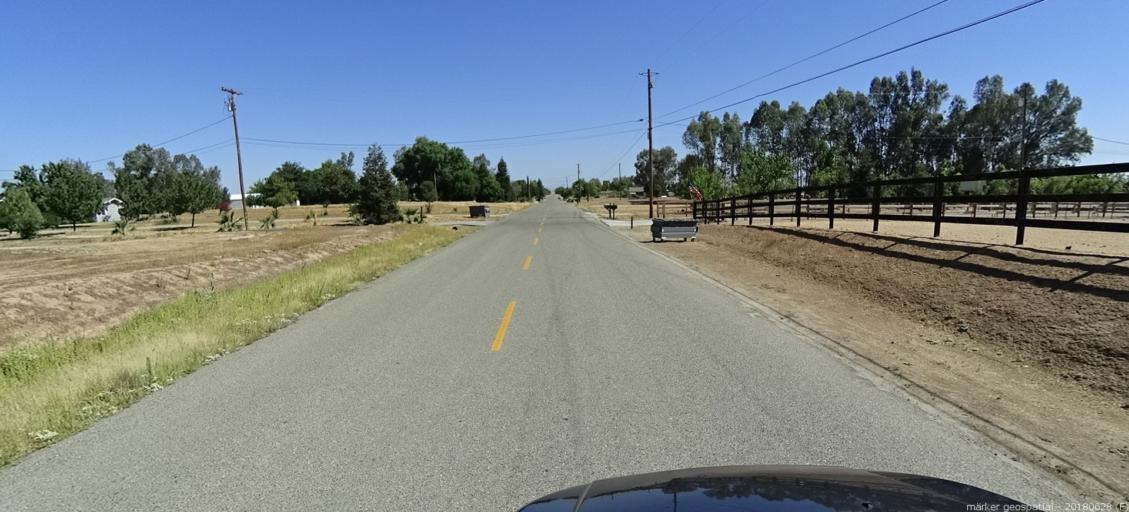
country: US
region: California
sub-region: Madera County
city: Bonadelle Ranchos-Madera Ranchos
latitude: 36.9826
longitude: -119.8686
